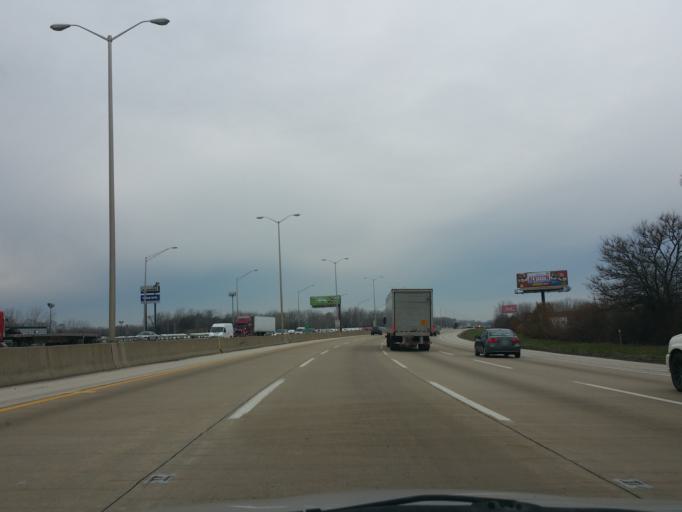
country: US
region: Illinois
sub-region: Cook County
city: Crestwood
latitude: 41.6659
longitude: -87.7503
